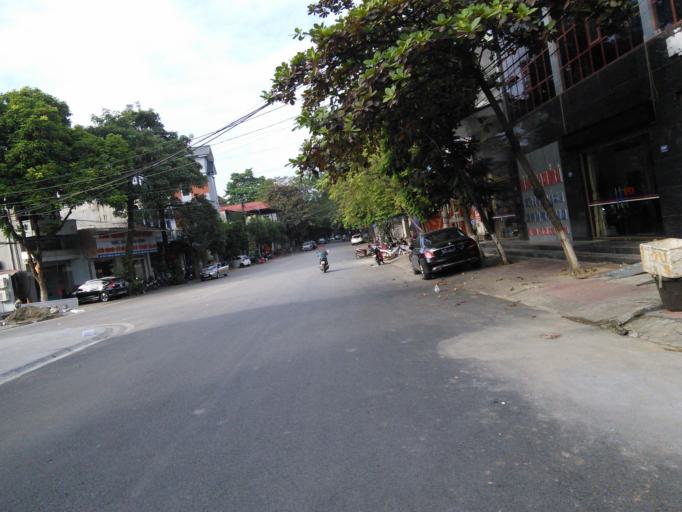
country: VN
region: Lao Cai
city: Lao Cai
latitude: 22.4947
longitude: 103.9691
